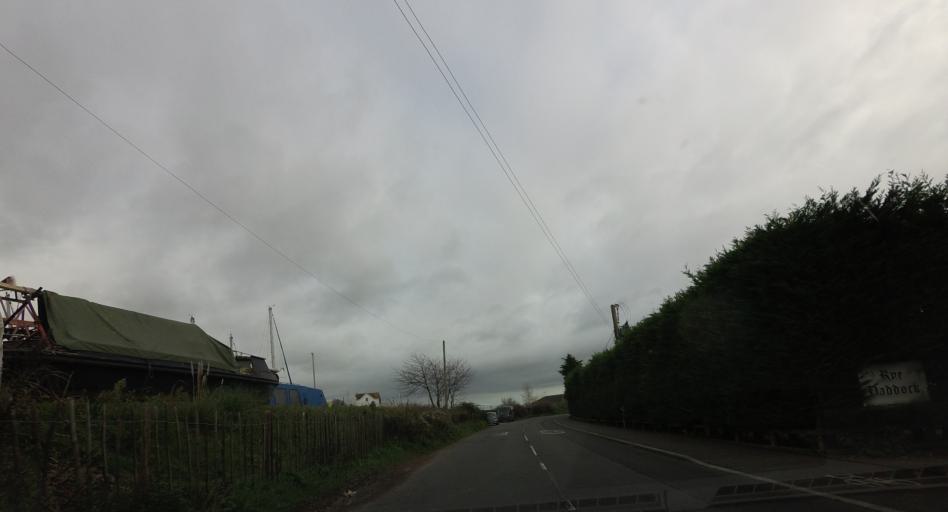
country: GB
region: England
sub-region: East Sussex
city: Rye
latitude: 50.9469
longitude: 0.7333
